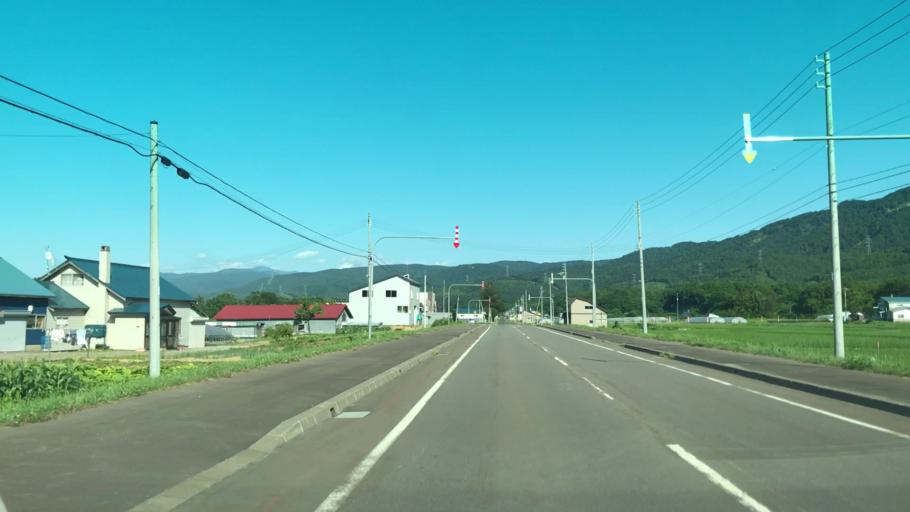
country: JP
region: Hokkaido
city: Yoichi
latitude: 43.0380
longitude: 140.7398
